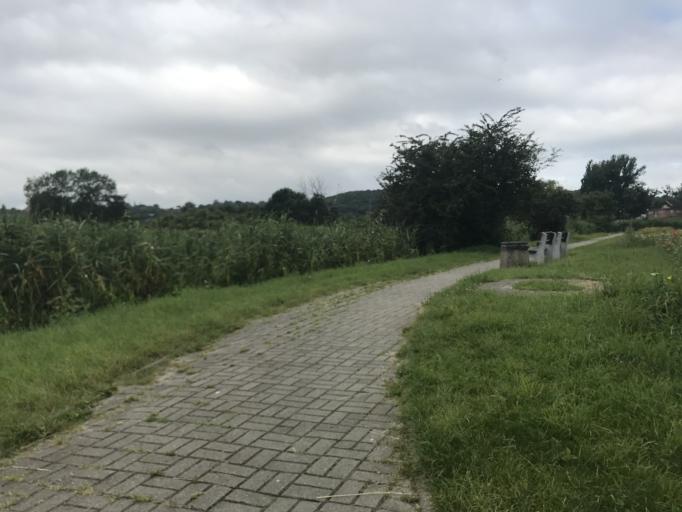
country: PL
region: Pomeranian Voivodeship
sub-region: Gdansk
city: Gdansk
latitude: 54.3375
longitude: 18.6541
